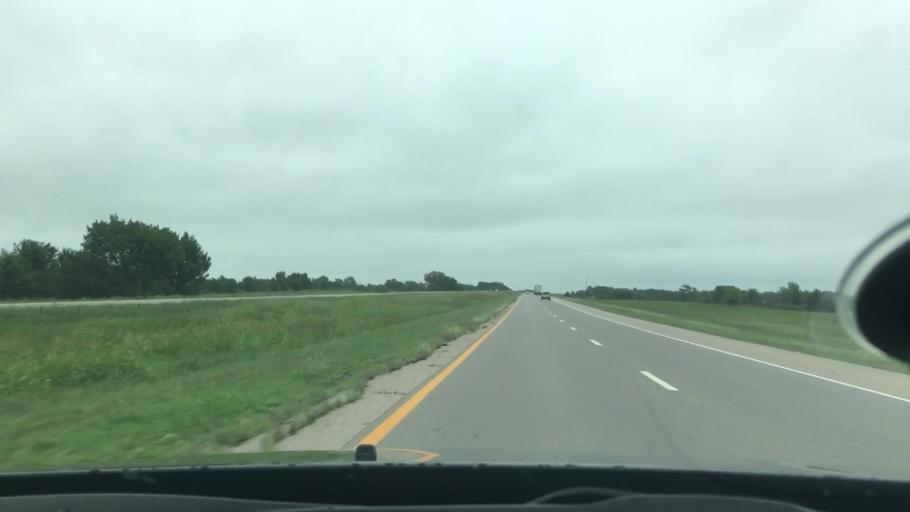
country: US
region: Oklahoma
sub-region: Okfuskee County
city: Okemah
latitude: 35.4249
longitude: -96.2723
